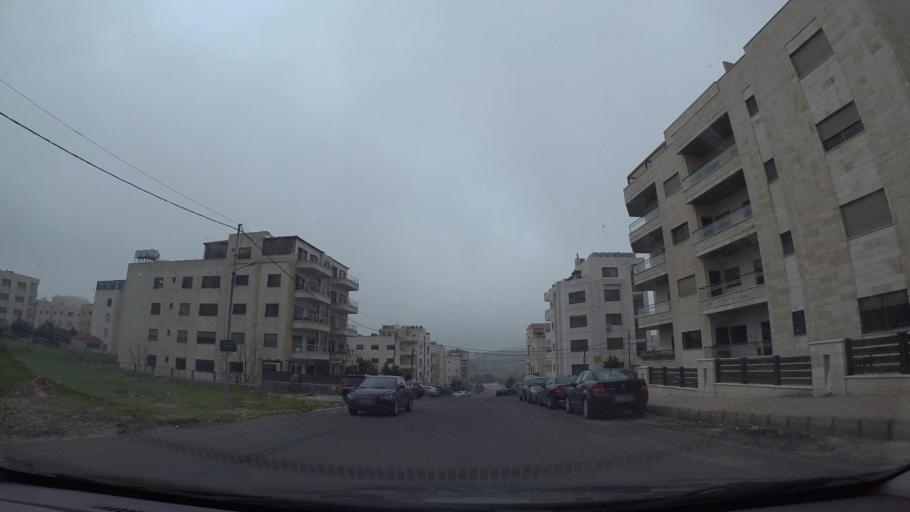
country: JO
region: Amman
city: Wadi as Sir
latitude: 31.9393
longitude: 35.8569
